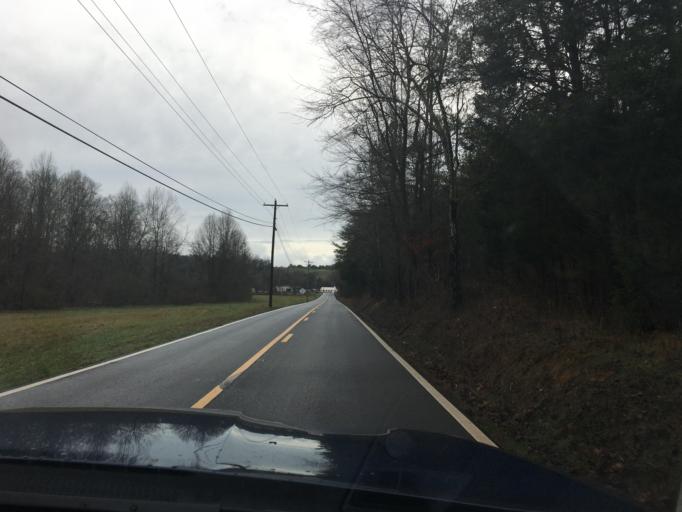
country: US
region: Tennessee
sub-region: McMinn County
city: Englewood
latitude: 35.4072
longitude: -84.4564
